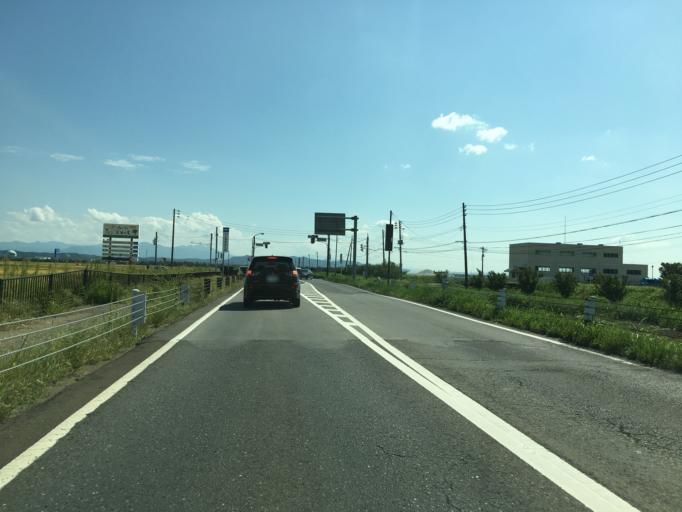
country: JP
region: Niigata
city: Kameda-honcho
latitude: 37.8329
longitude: 139.0968
